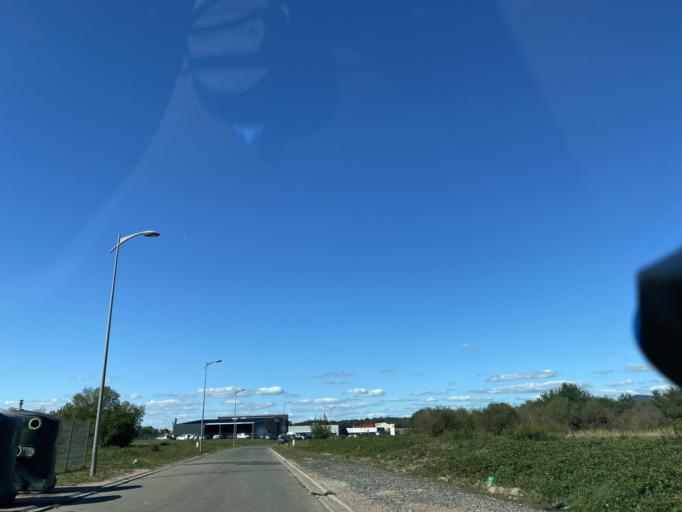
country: FR
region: Auvergne
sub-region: Departement du Puy-de-Dome
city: Peschadoires
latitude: 45.8353
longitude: 3.5142
